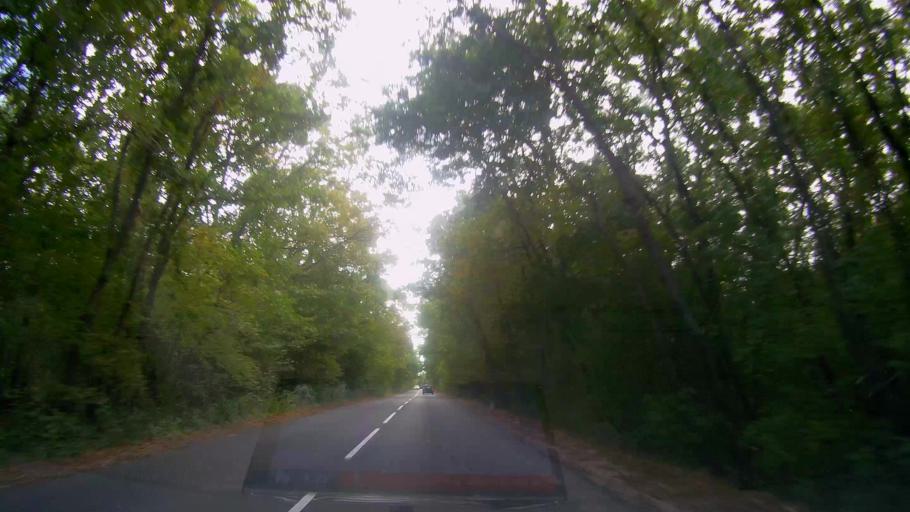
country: BG
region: Burgas
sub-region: Obshtina Primorsko
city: Primorsko
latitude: 42.2975
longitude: 27.7296
